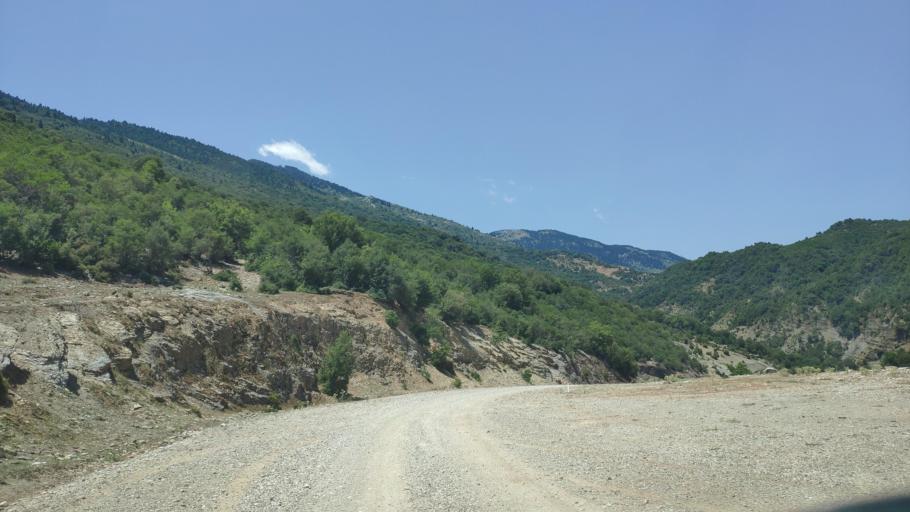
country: GR
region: Thessaly
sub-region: Nomos Kardhitsas
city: Anthiro
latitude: 39.1646
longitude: 21.3741
